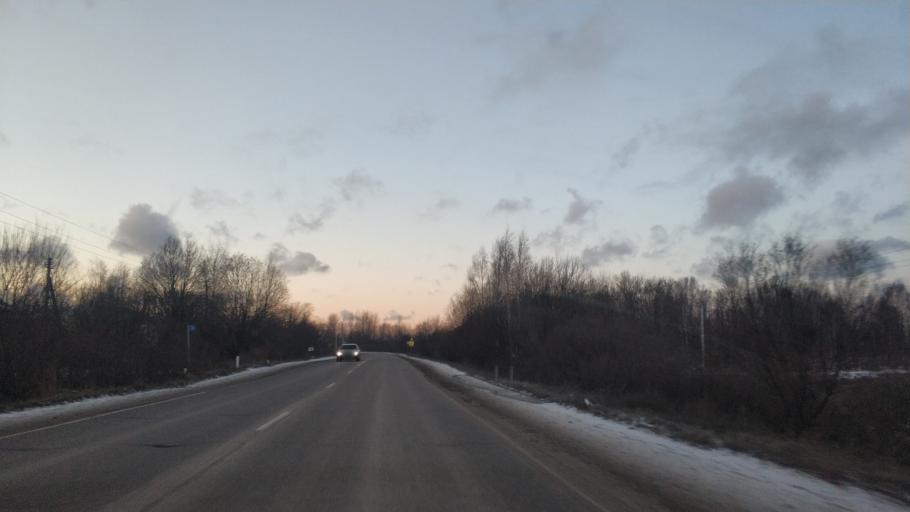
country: RU
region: St.-Petersburg
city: Pontonnyy
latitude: 59.8054
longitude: 30.6246
